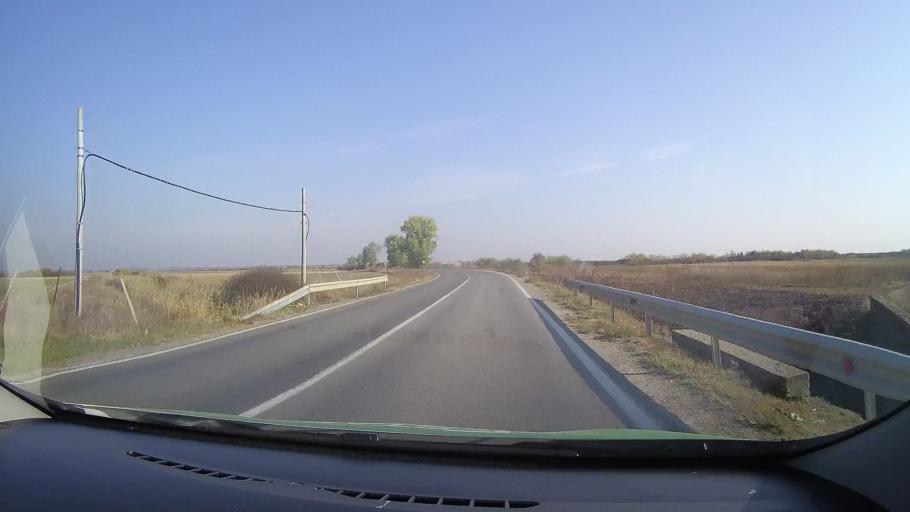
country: RO
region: Arad
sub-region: Comuna Pilu
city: Pilu
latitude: 46.5974
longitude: 21.3489
